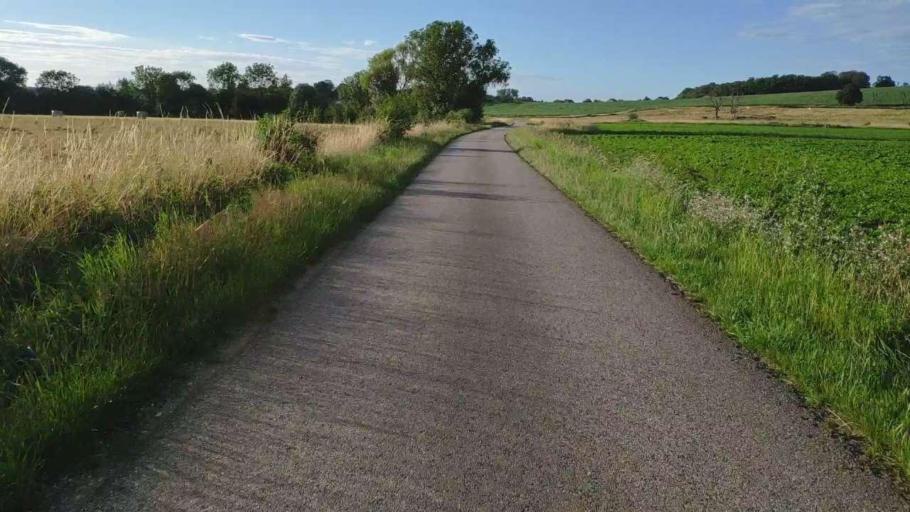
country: FR
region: Franche-Comte
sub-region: Departement du Jura
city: Bletterans
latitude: 46.7748
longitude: 5.4963
